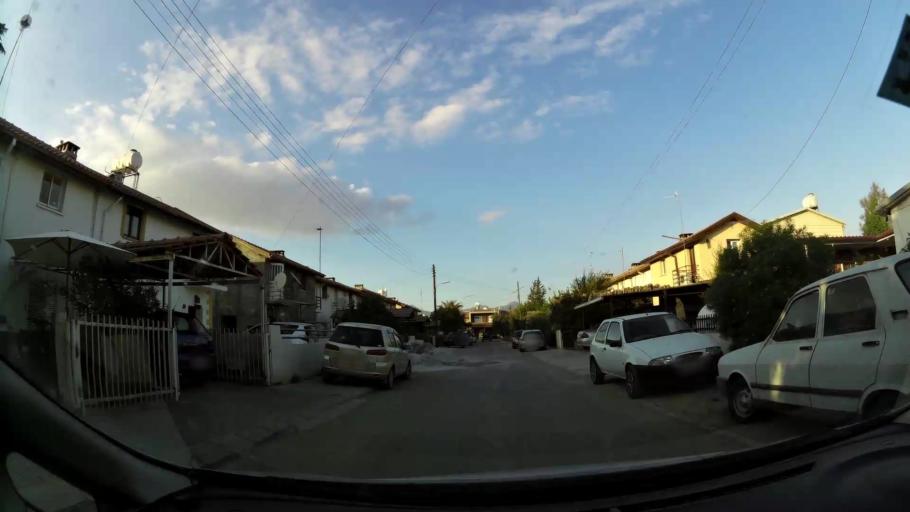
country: CY
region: Lefkosia
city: Nicosia
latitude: 35.1860
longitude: 33.3668
